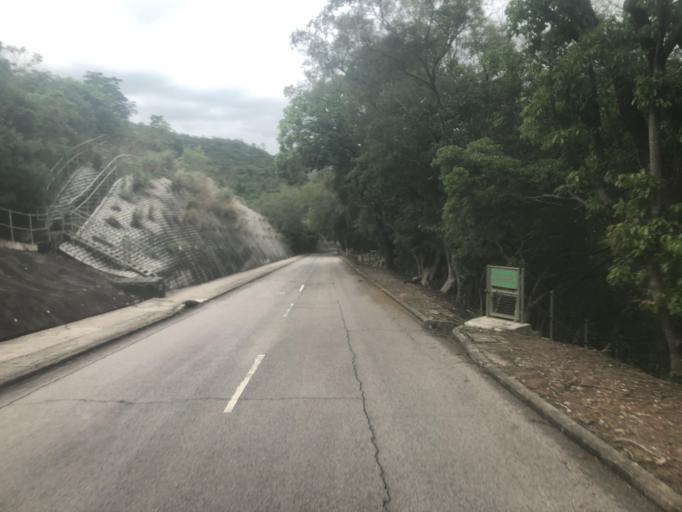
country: HK
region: Sai Kung
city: Sai Kung
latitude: 22.3969
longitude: 114.3266
